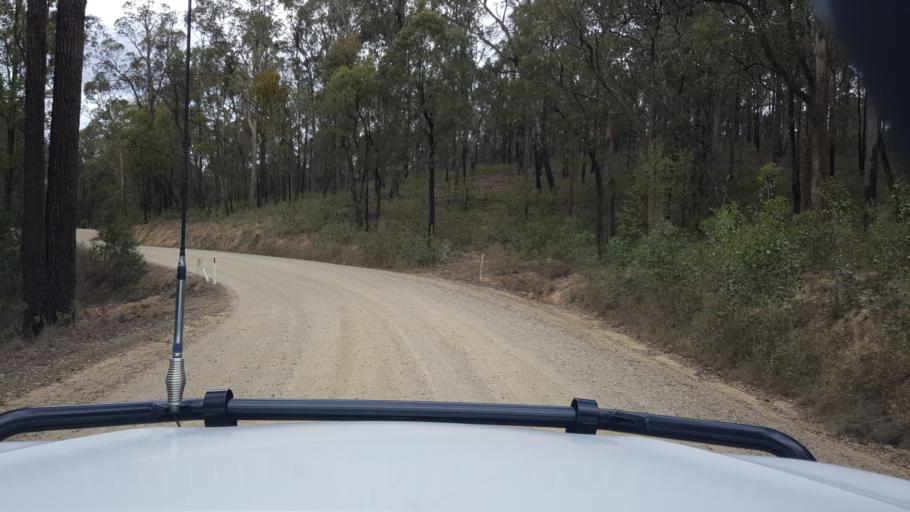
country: AU
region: Victoria
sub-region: East Gippsland
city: Bairnsdale
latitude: -37.6991
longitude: 147.5845
